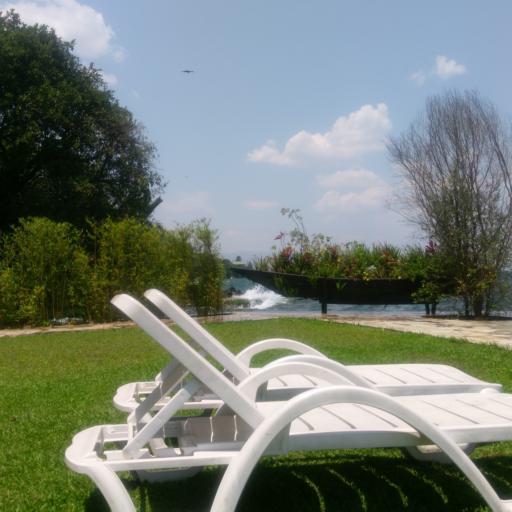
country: CD
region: Nord Kivu
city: Goma
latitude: -1.6750
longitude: 29.2034
